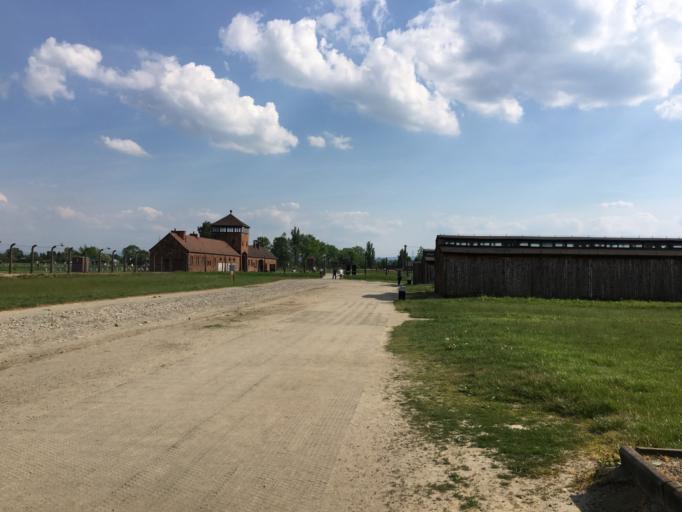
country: PL
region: Lesser Poland Voivodeship
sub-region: Powiat oswiecimski
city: Brzezinka
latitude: 50.0358
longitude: 19.1803
